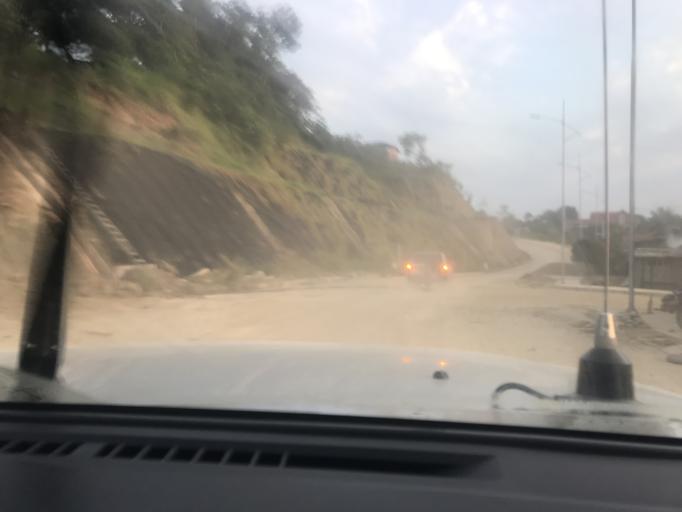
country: BO
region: El Beni
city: Rurrenabaque
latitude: -14.4408
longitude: -67.5366
